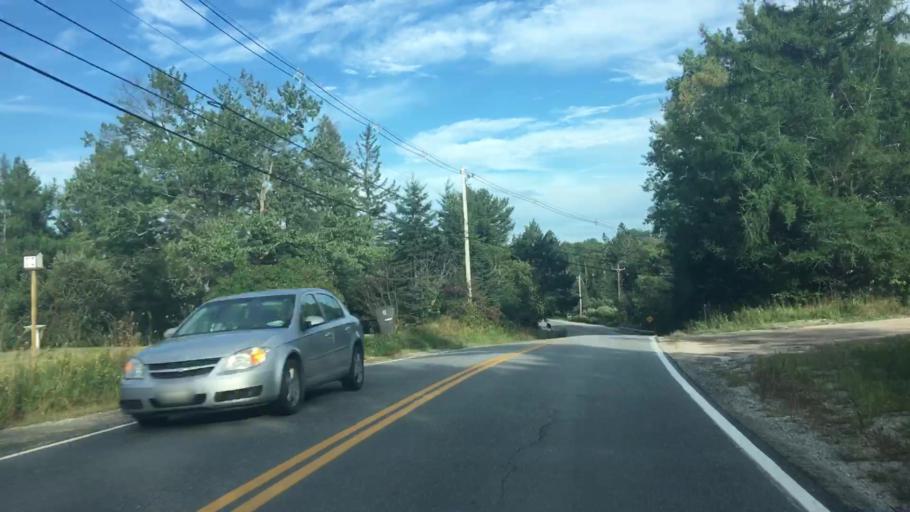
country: US
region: Maine
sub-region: Hancock County
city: Trenton
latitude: 44.4378
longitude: -68.3939
